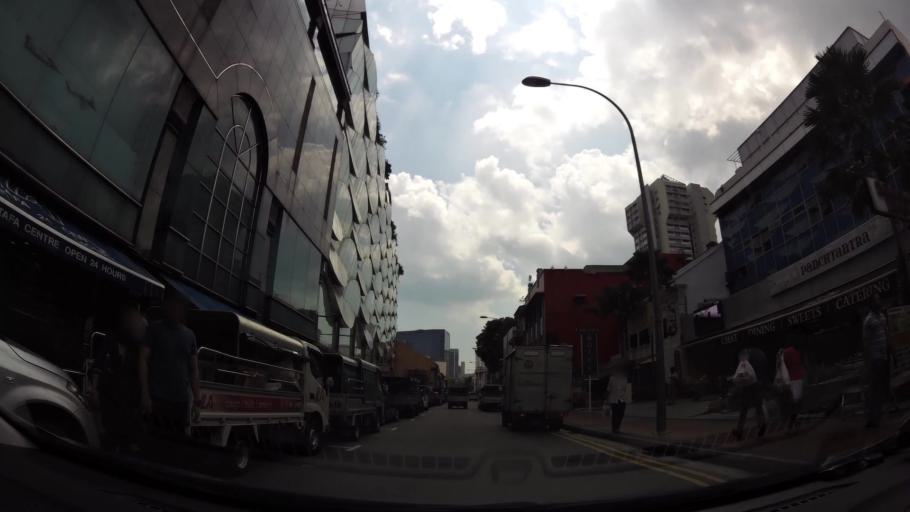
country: SG
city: Singapore
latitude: 1.3094
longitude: 103.8559
